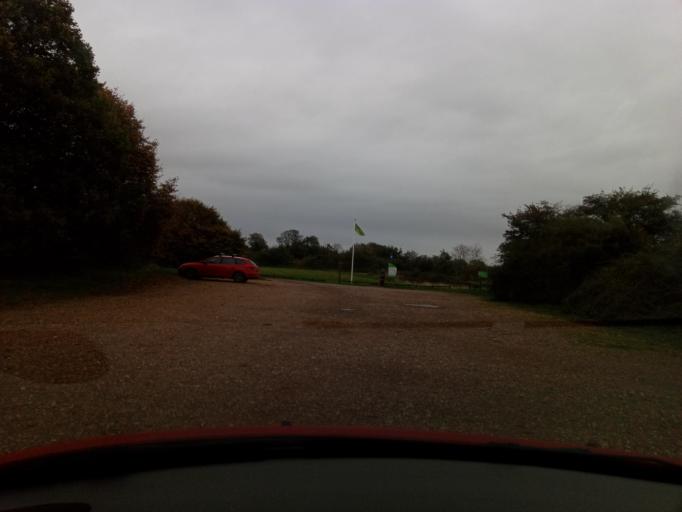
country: GB
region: England
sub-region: Essex
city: Brightlingsea
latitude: 51.7921
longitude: 0.9933
